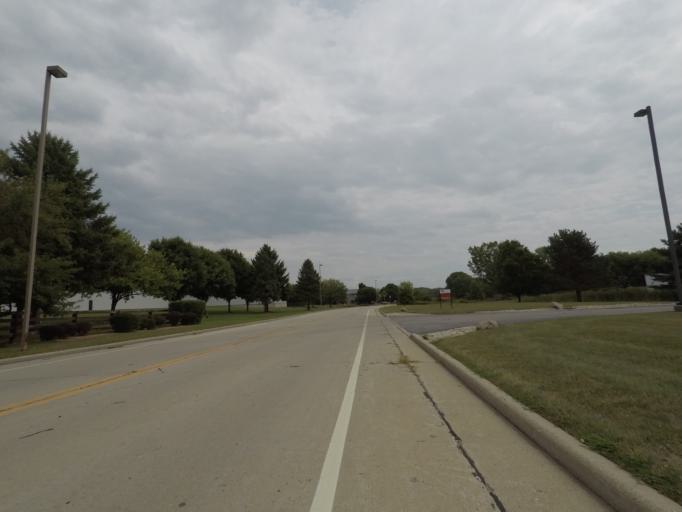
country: US
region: Wisconsin
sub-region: Jefferson County
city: Fort Atkinson
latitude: 42.9427
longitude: -88.8348
